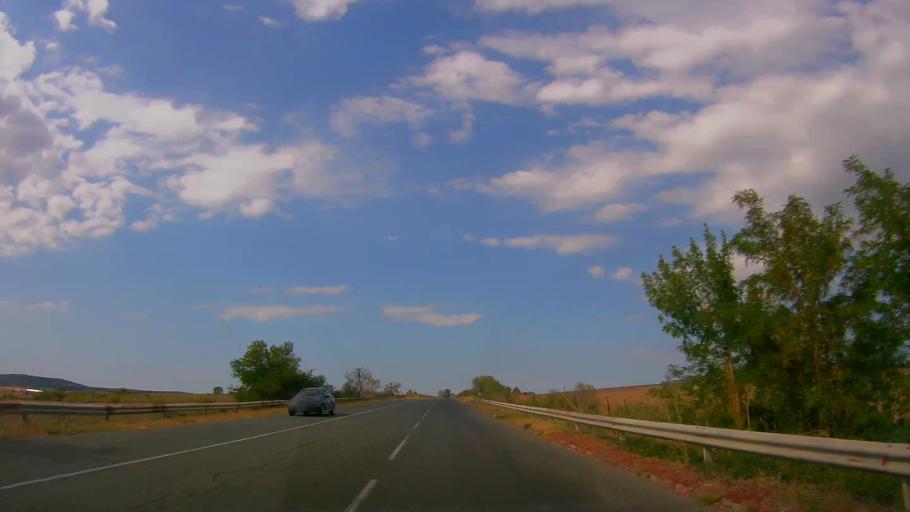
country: BG
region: Burgas
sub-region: Obshtina Aytos
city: Aytos
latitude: 42.6975
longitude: 27.2019
